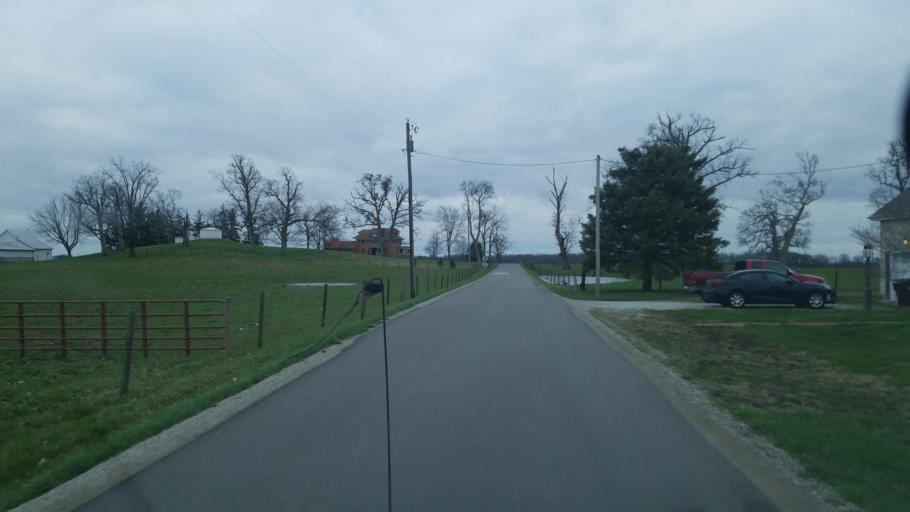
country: US
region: Ohio
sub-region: Fayette County
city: Jeffersonville
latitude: 39.5869
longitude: -83.5161
